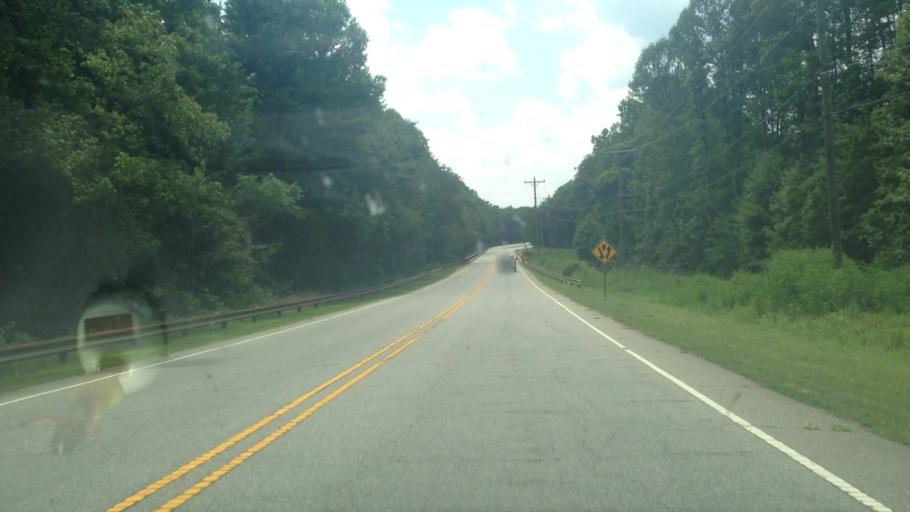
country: US
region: North Carolina
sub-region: Forsyth County
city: Rural Hall
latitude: 36.2037
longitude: -80.2875
